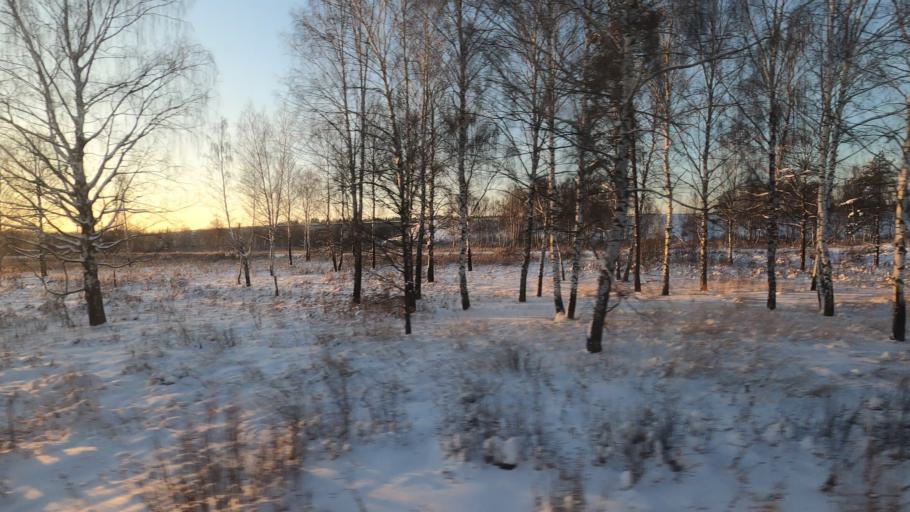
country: RU
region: Moskovskaya
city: Orud'yevo
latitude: 56.4055
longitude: 37.4947
